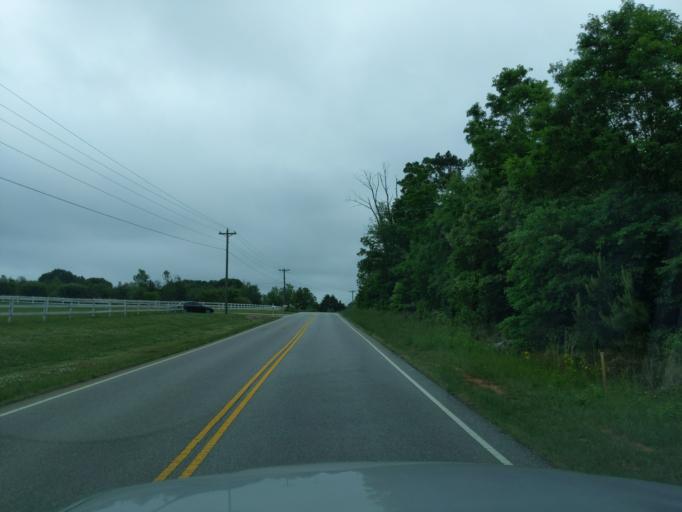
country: US
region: South Carolina
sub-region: Greenville County
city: Five Forks
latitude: 34.8568
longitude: -82.2027
